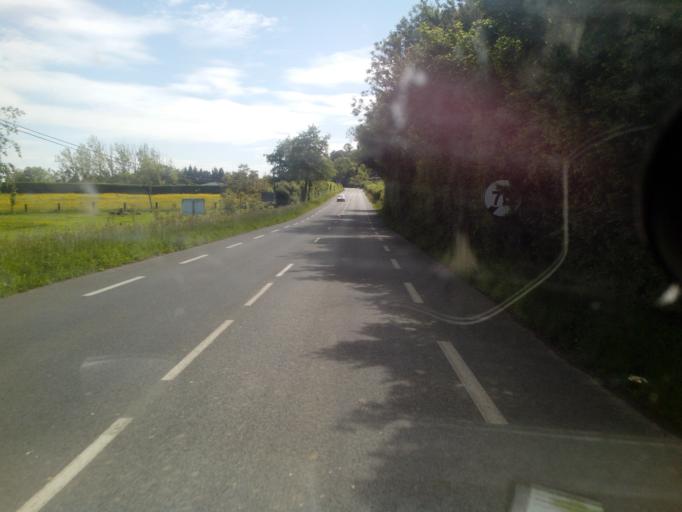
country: FR
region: Lower Normandy
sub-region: Departement du Calvados
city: Saint-Gatien-des-Bois
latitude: 49.2747
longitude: 0.1704
